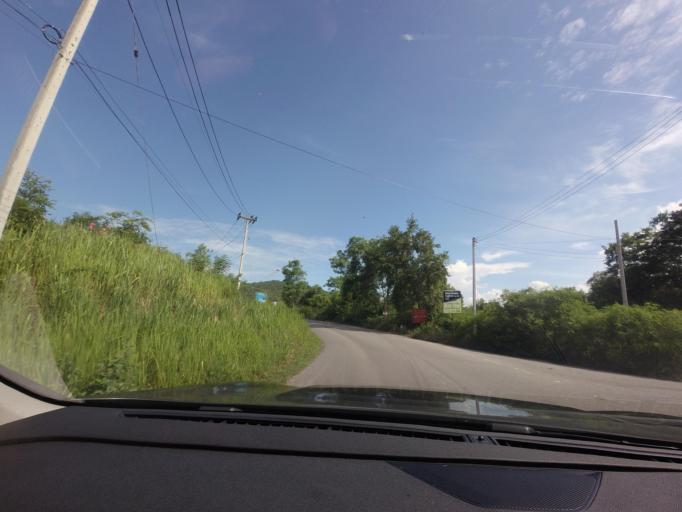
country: TH
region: Prachuap Khiri Khan
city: Hua Hin
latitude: 12.4928
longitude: 99.9414
